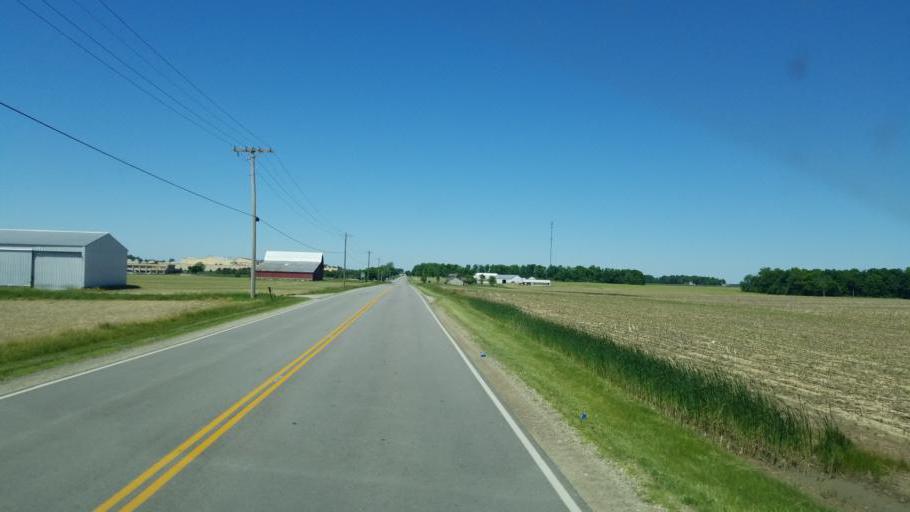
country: US
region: Ohio
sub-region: Shelby County
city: Anna
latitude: 40.3806
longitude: -84.1779
